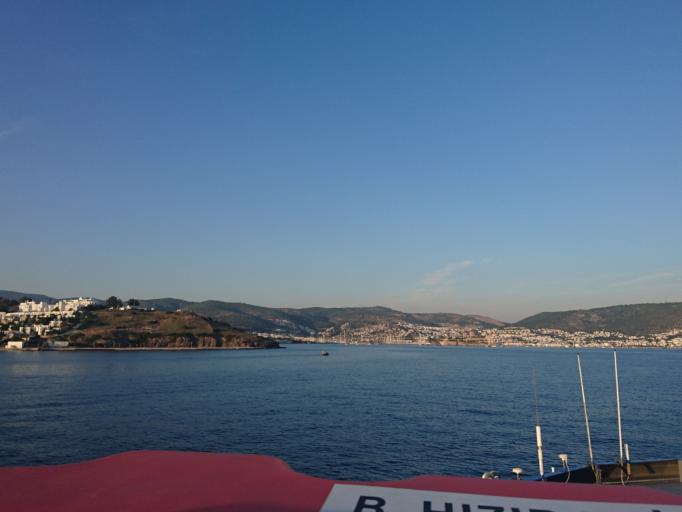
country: TR
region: Mugla
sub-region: Bodrum
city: Bodrum
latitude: 37.0165
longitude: 27.4177
